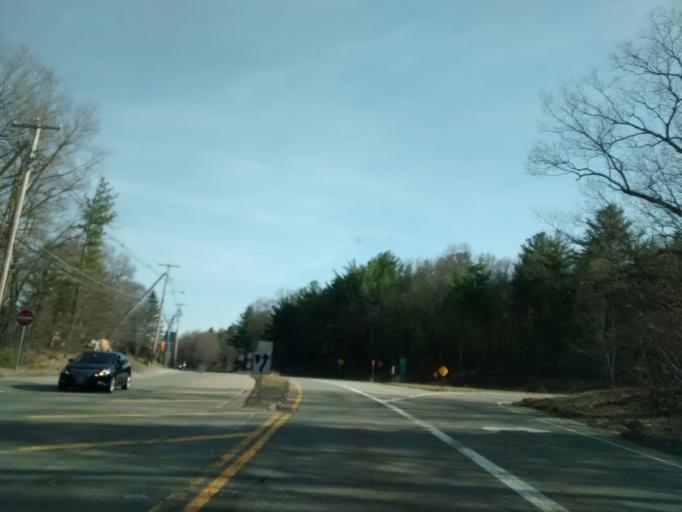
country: US
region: Massachusetts
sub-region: Worcester County
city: Uxbridge
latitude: 42.0443
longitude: -71.6221
